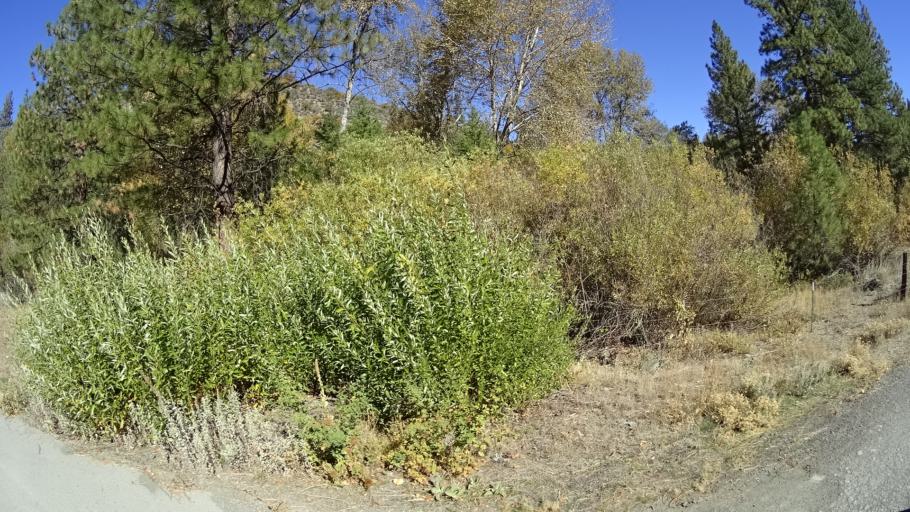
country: US
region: California
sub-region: Siskiyou County
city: Weed
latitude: 41.2955
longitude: -122.8086
